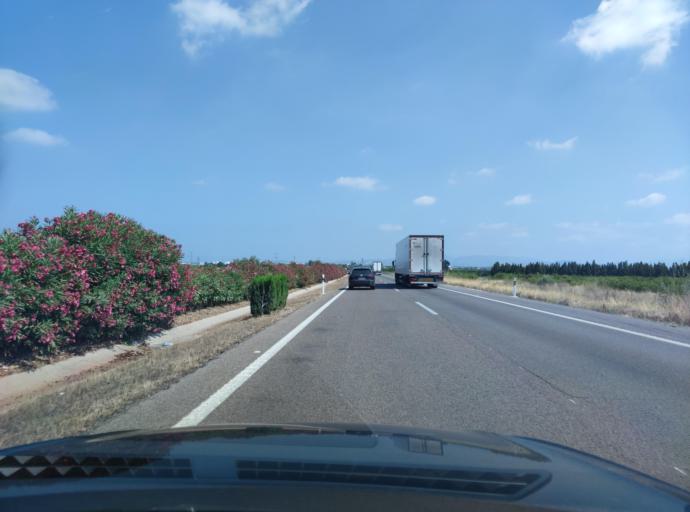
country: ES
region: Valencia
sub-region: Provincia de Castello
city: Alquerias del Nino Perdido
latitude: 39.9134
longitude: -0.1350
